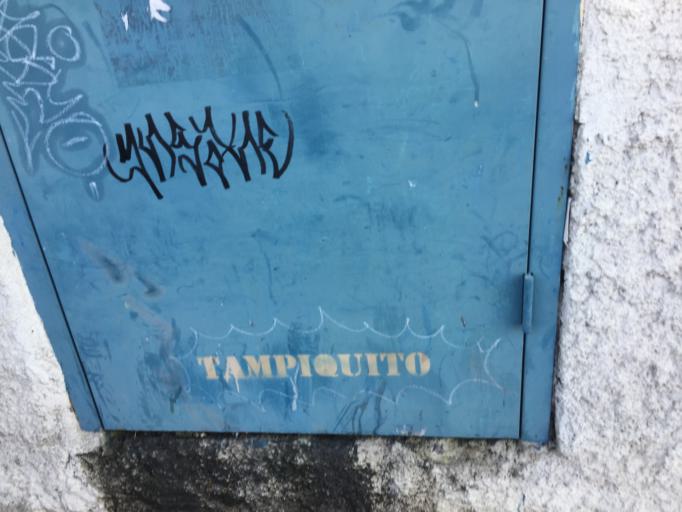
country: MX
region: Nuevo Leon
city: Garza Garcia
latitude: 25.6513
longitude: -100.3732
